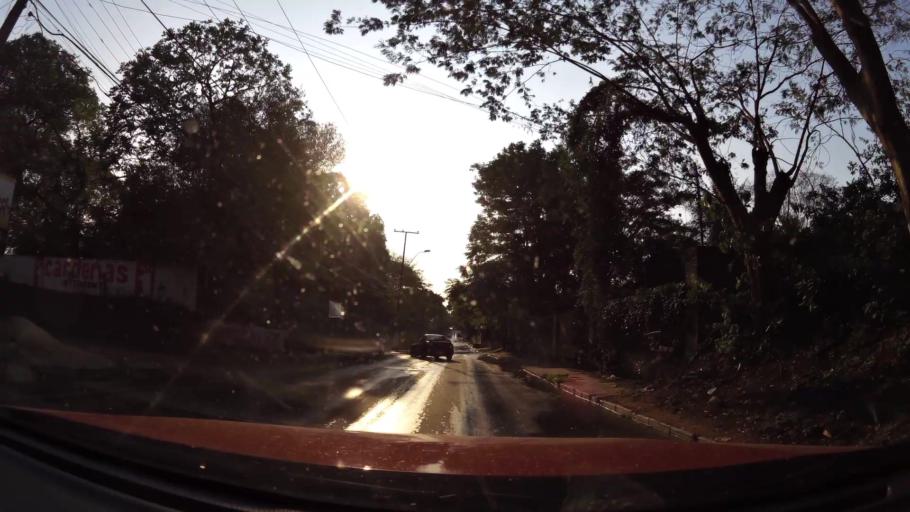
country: PY
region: Central
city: Lambare
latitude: -25.3559
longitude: -57.6044
